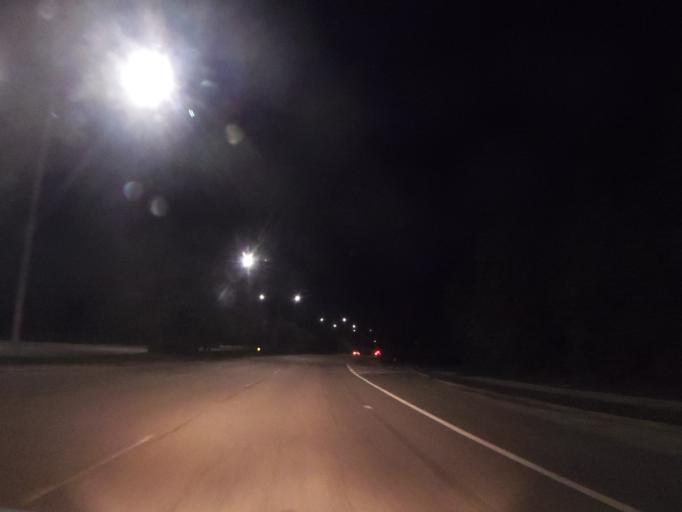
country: US
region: Florida
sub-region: Duval County
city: Jacksonville Beach
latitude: 30.2660
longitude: -81.5268
